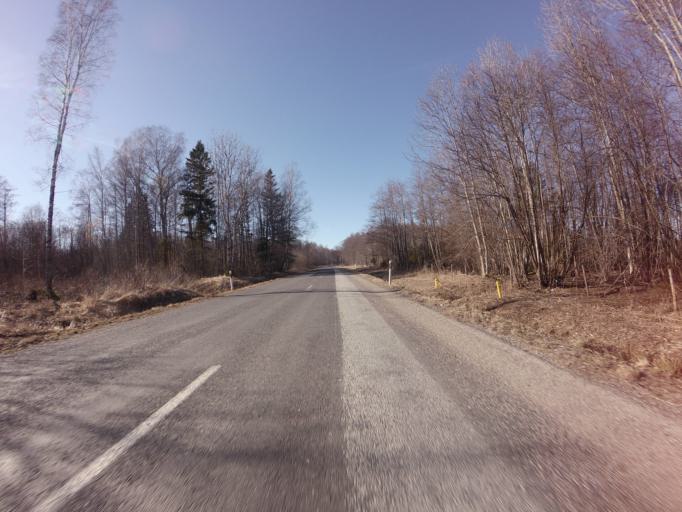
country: EE
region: Saare
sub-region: Kuressaare linn
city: Kuressaare
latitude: 58.5780
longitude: 22.6351
